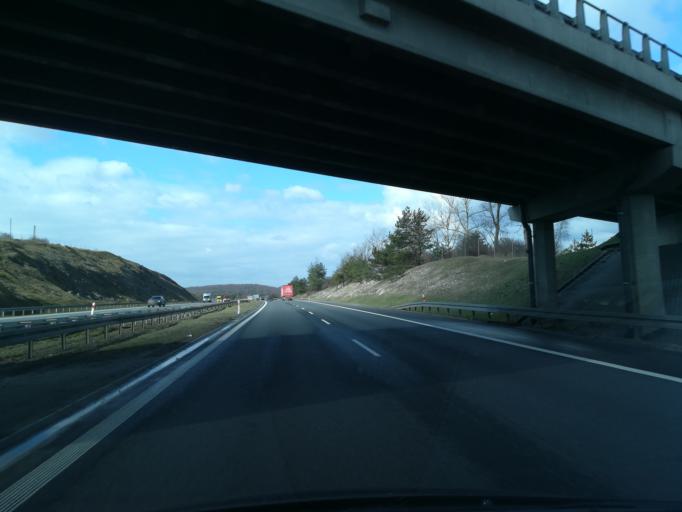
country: PL
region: Lesser Poland Voivodeship
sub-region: Powiat krakowski
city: Zalas
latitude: 50.0931
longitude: 19.6243
